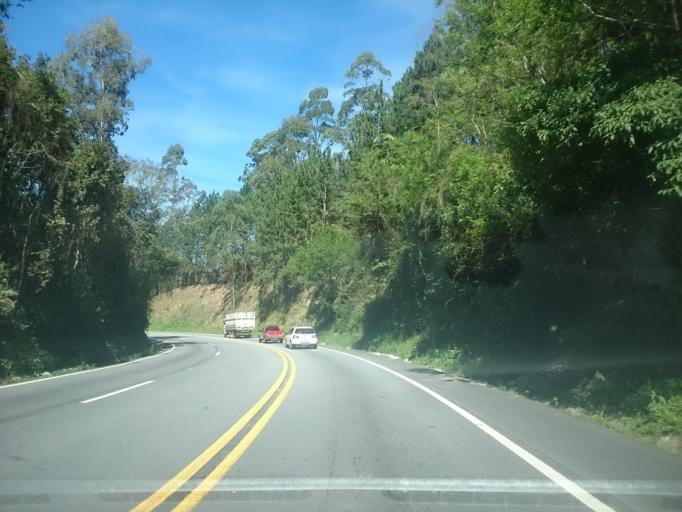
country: BR
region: Santa Catarina
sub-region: Santo Amaro Da Imperatriz
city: Santo Amaro da Imperatriz
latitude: -27.7152
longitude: -48.9441
